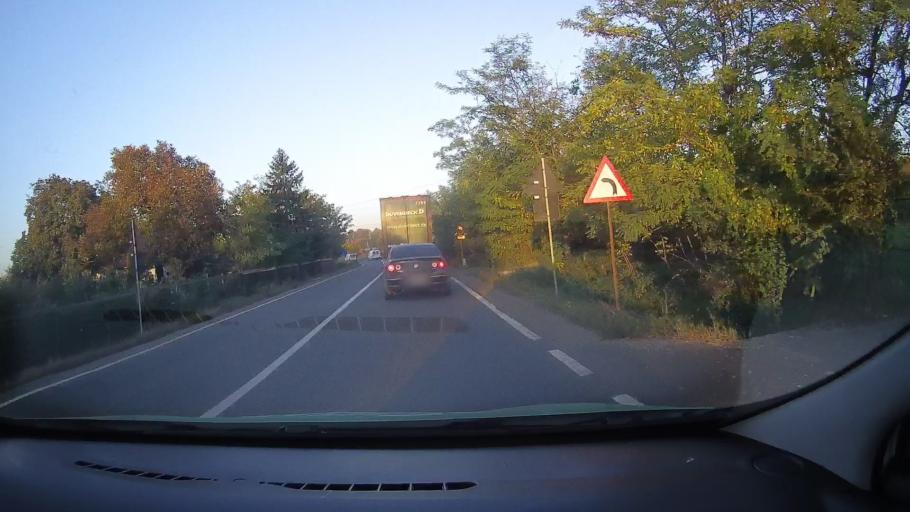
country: RO
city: Dioszeg
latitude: 47.2916
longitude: 22.0088
